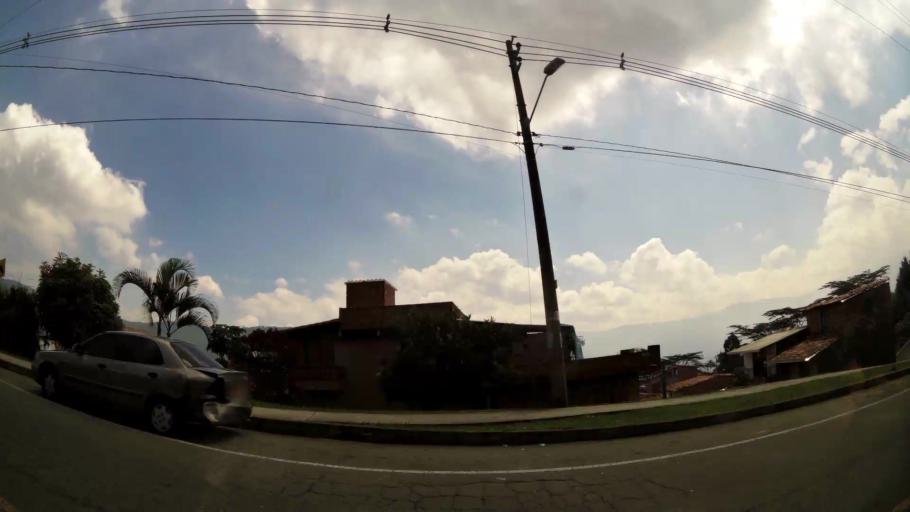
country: CO
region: Antioquia
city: La Estrella
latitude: 6.1738
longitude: -75.6520
